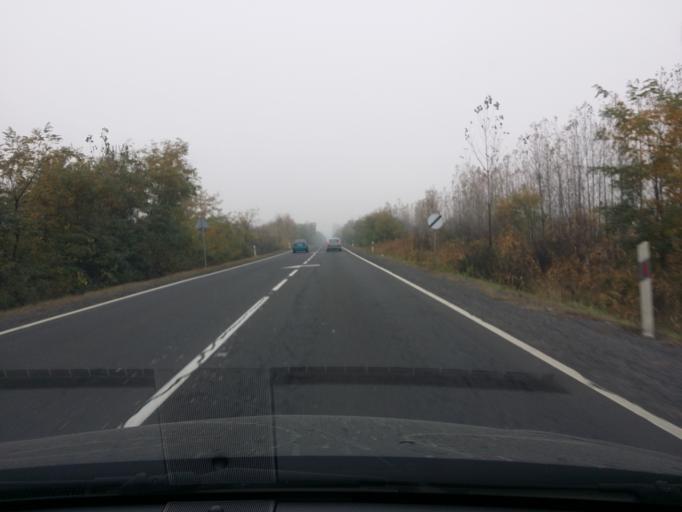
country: HU
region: Szabolcs-Szatmar-Bereg
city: Nyirbogdany
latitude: 48.0240
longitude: 21.8456
